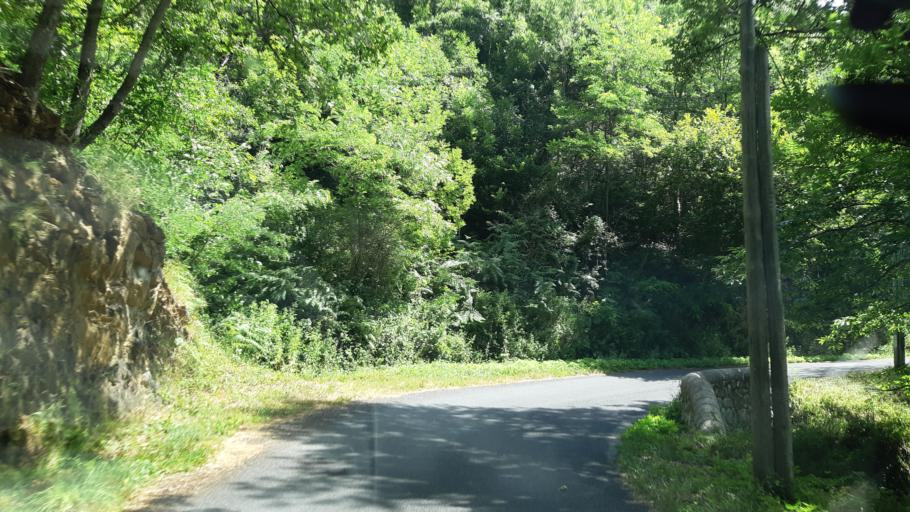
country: FR
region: Languedoc-Roussillon
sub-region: Departement des Pyrenees-Orientales
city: Arles
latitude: 42.5322
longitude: 2.6110
